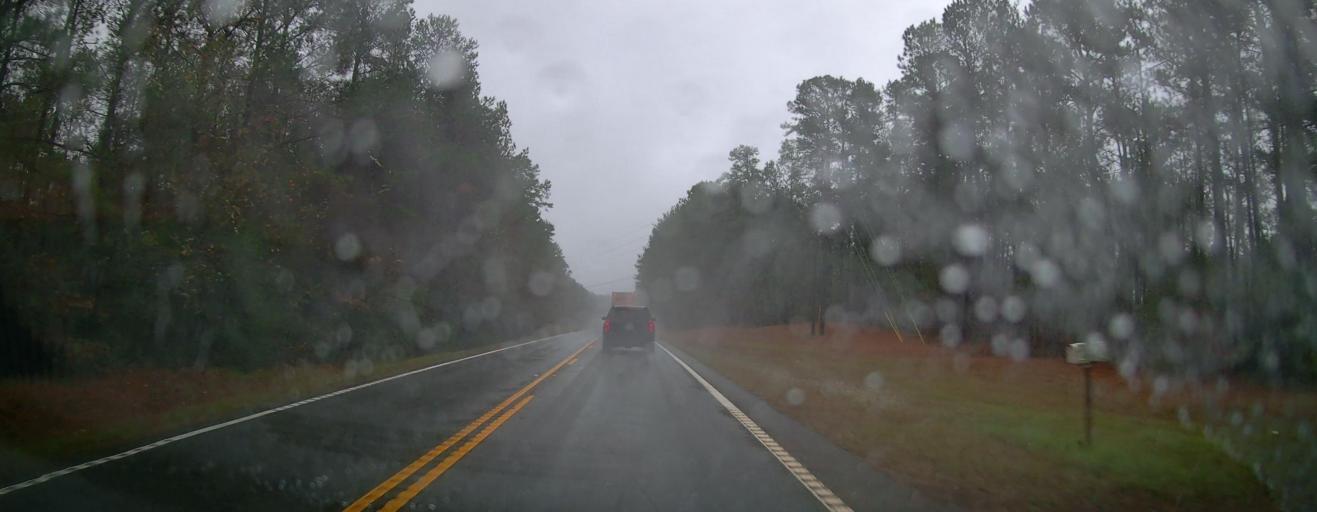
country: US
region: Georgia
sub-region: Putnam County
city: Eatonton
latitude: 33.1686
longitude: -83.4418
